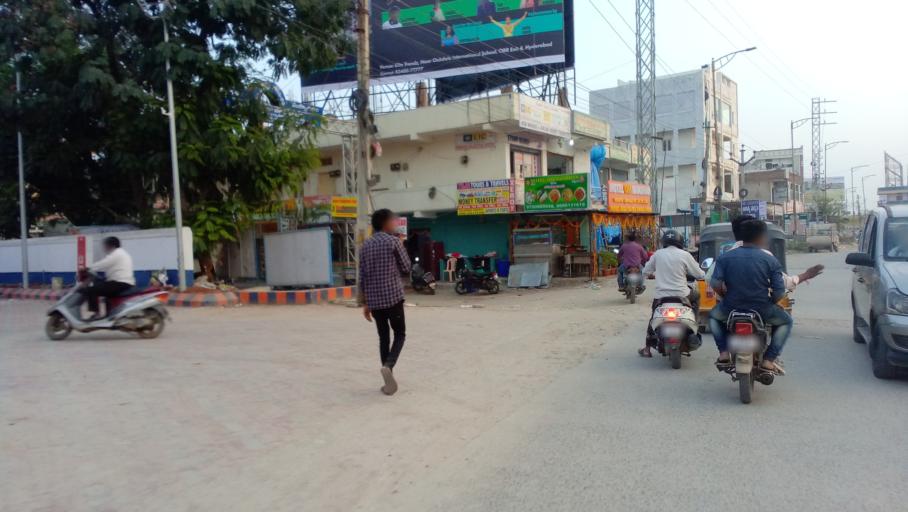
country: IN
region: Telangana
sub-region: Medak
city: Serilingampalle
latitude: 17.5196
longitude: 78.2998
